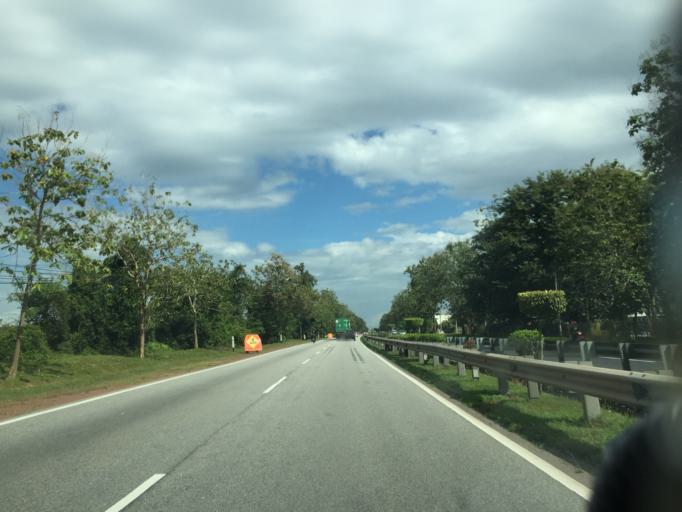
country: MY
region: Kedah
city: Jitra
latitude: 6.3411
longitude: 100.4204
